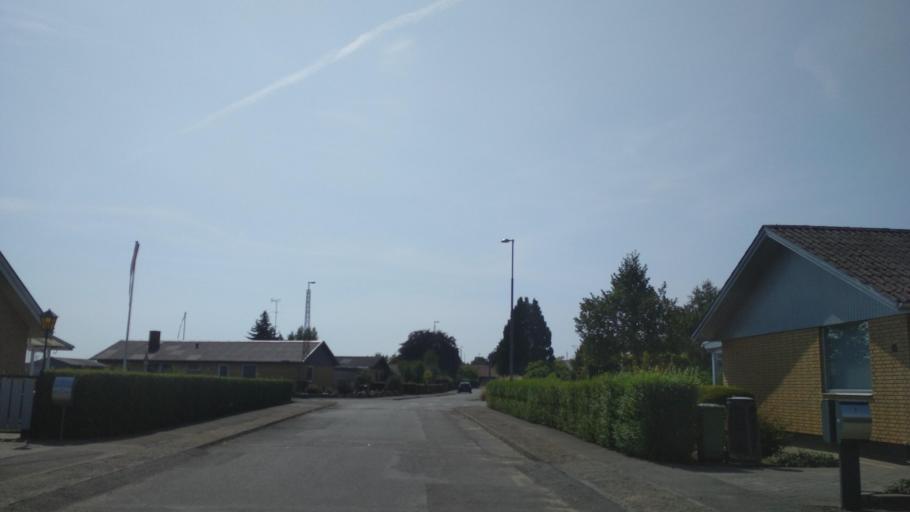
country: DK
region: Capital Region
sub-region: Bornholm Kommune
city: Akirkeby
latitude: 55.0684
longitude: 14.9282
